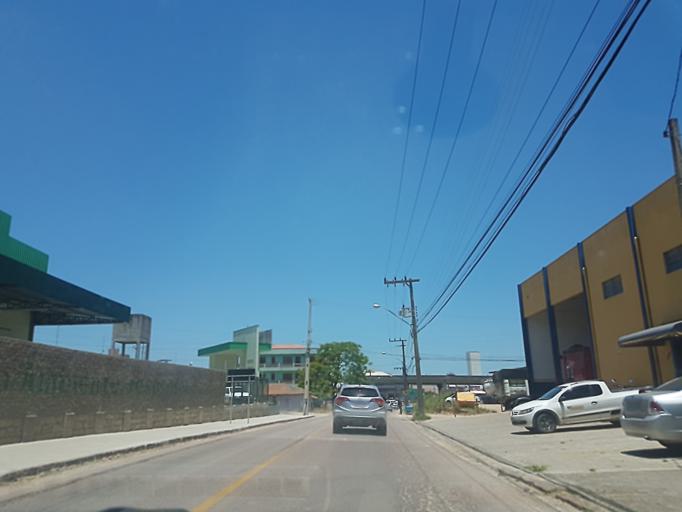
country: BR
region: Santa Catarina
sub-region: Tubarao
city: Tubarao
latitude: -28.4750
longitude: -49.0309
